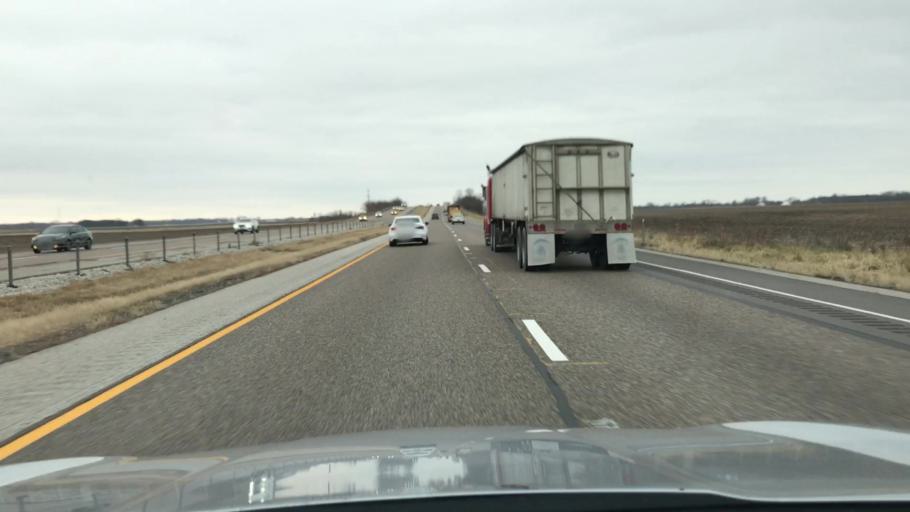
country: US
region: Illinois
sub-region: Madison County
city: Edwardsville
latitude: 38.8303
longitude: -89.8795
